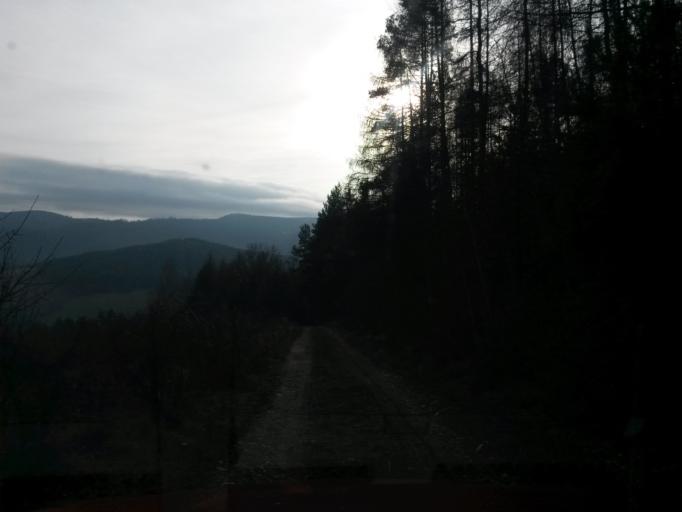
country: SK
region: Kosicky
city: Dobsina
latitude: 48.7310
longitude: 20.4079
